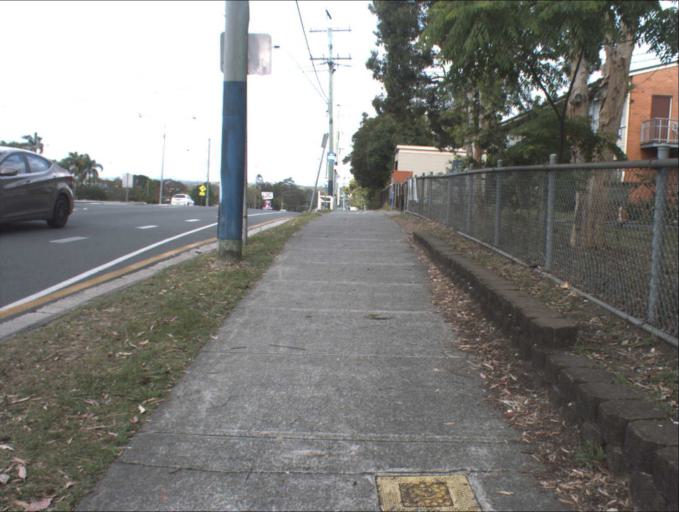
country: AU
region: Queensland
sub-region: Logan
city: Logan City
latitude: -27.6417
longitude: 153.1047
